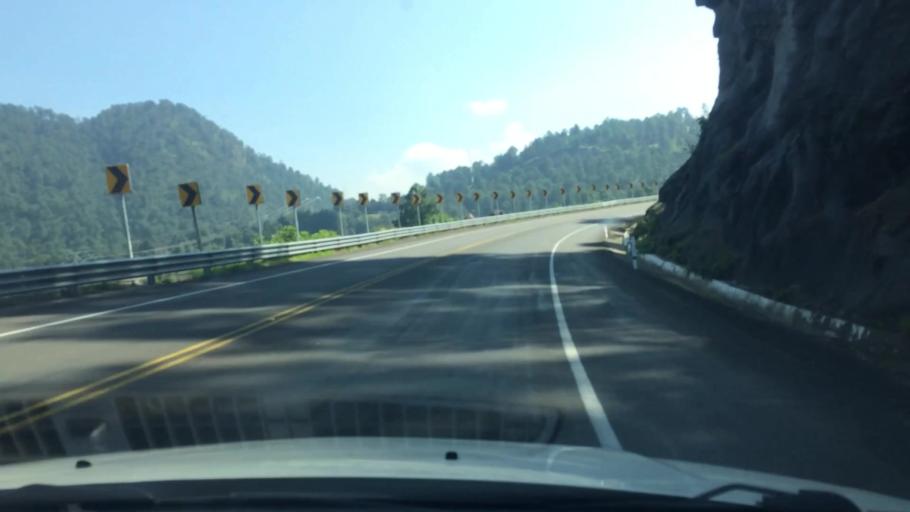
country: MX
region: Mexico
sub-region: Amanalco
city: Polvillos (San Bartolo Quinta Seccion)
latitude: 19.2283
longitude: -100.0819
